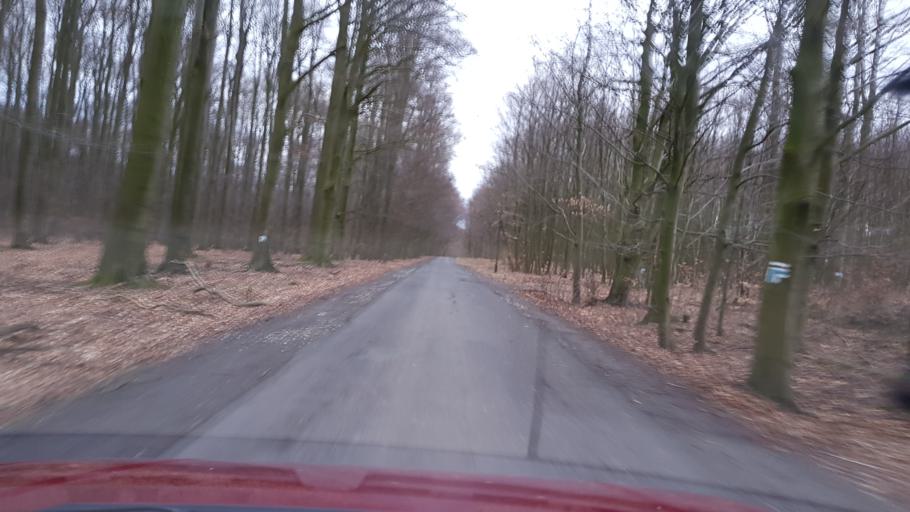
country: PL
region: West Pomeranian Voivodeship
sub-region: Powiat gryfinski
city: Stare Czarnowo
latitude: 53.3212
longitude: 14.7082
